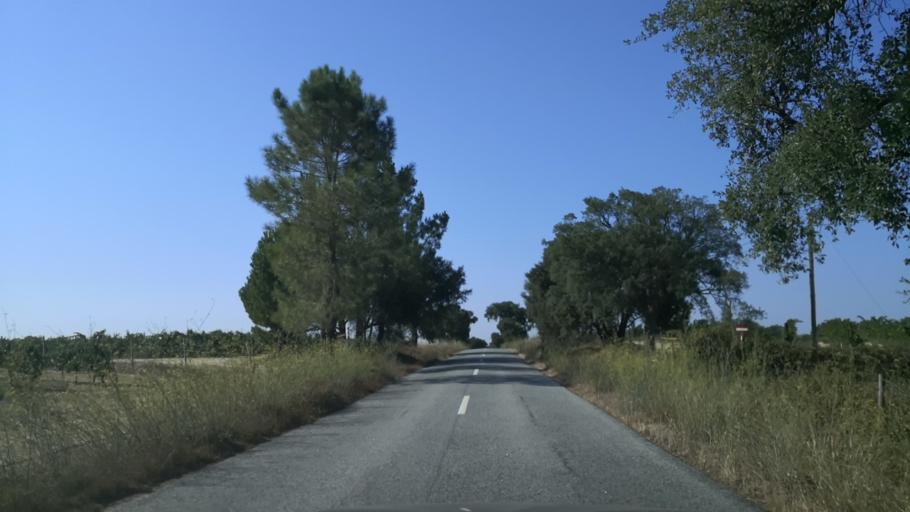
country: PT
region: Evora
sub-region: Vendas Novas
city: Vendas Novas
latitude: 38.7400
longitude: -8.6272
